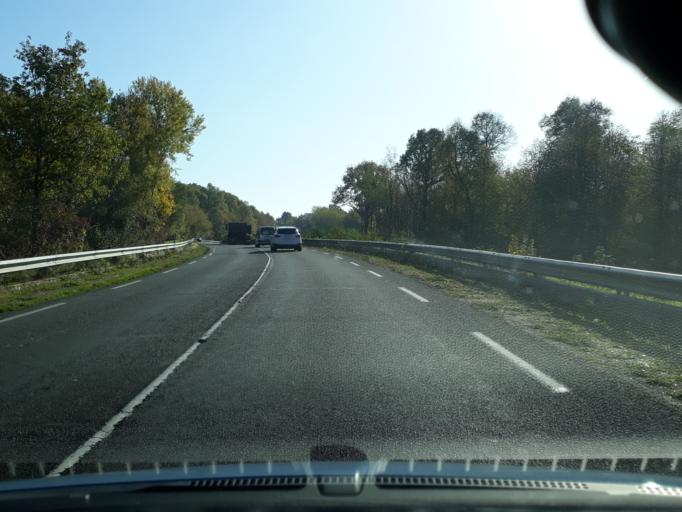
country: FR
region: Ile-de-France
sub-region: Departement de Seine-et-Marne
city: Livry-sur-Seine
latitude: 48.5019
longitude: 2.6847
